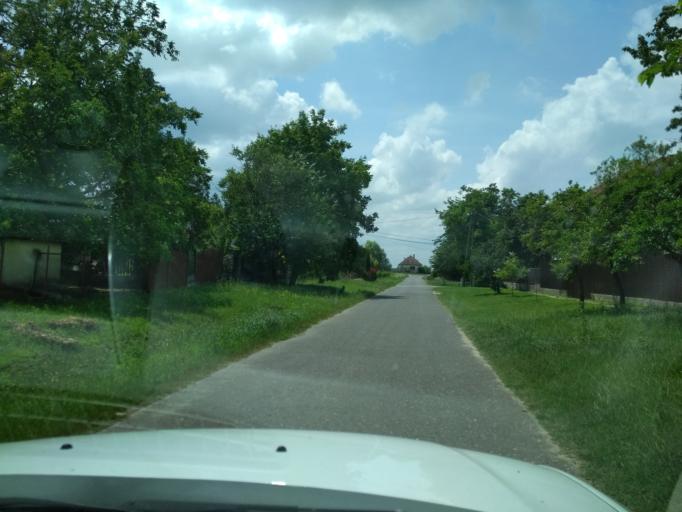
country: HU
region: Pest
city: Tapiosag
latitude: 47.4003
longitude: 19.6350
